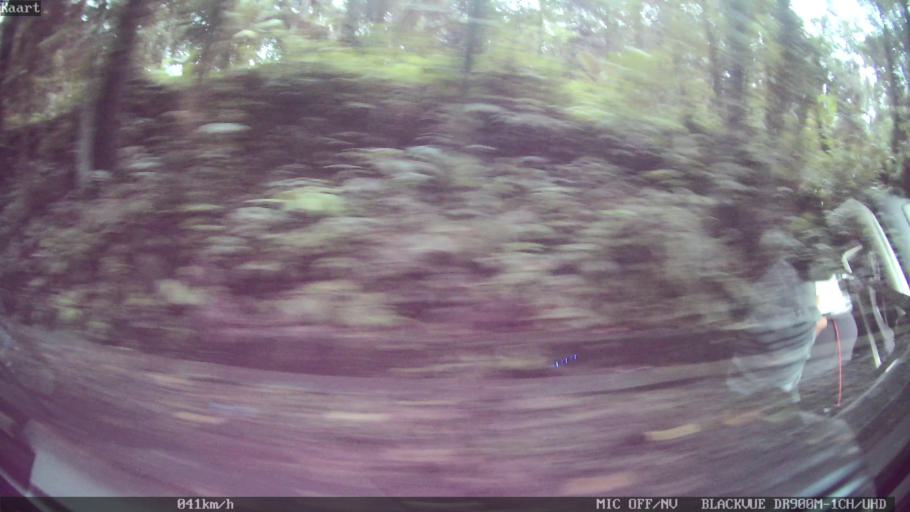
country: ID
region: Bali
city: Pegongan
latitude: -8.4806
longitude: 115.2283
